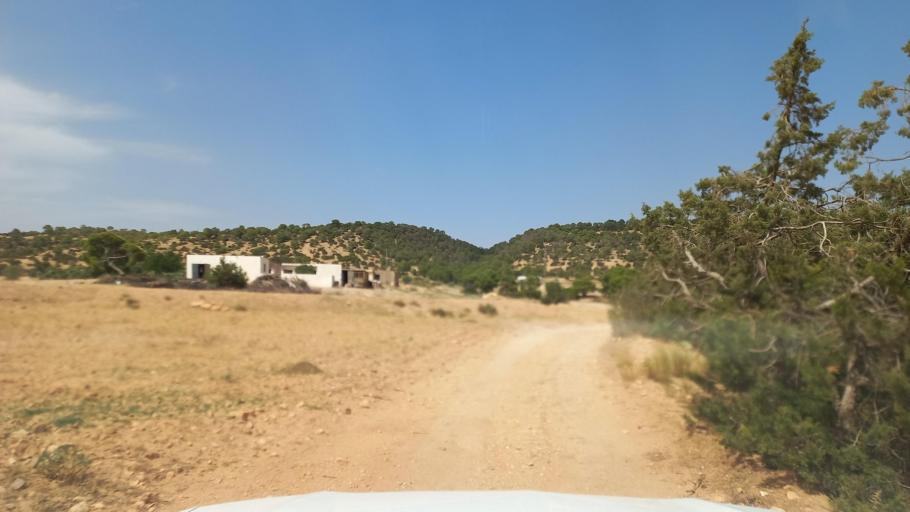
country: TN
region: Al Qasrayn
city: Kasserine
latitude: 35.3727
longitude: 8.8964
